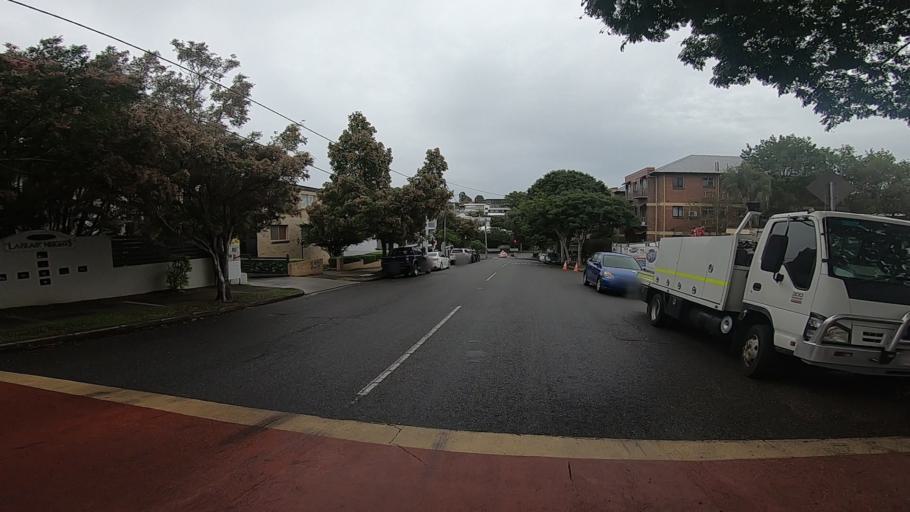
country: AU
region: Queensland
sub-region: Brisbane
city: Wooloowin
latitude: -27.4288
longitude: 153.0487
